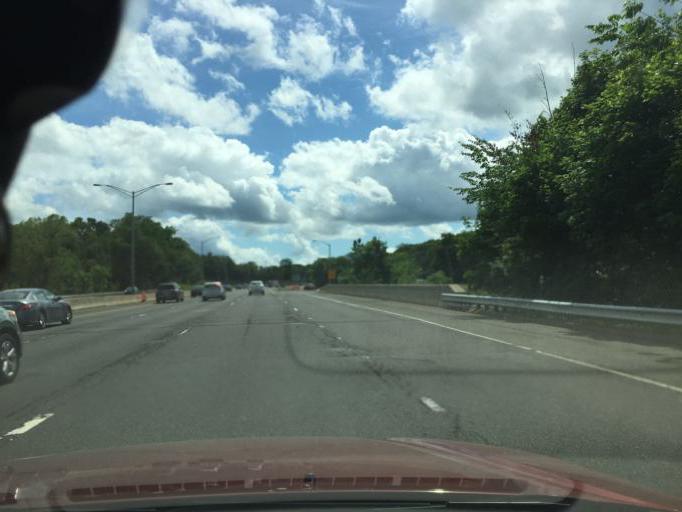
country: US
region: Connecticut
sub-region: Fairfield County
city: Danbury
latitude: 41.4057
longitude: -73.4607
